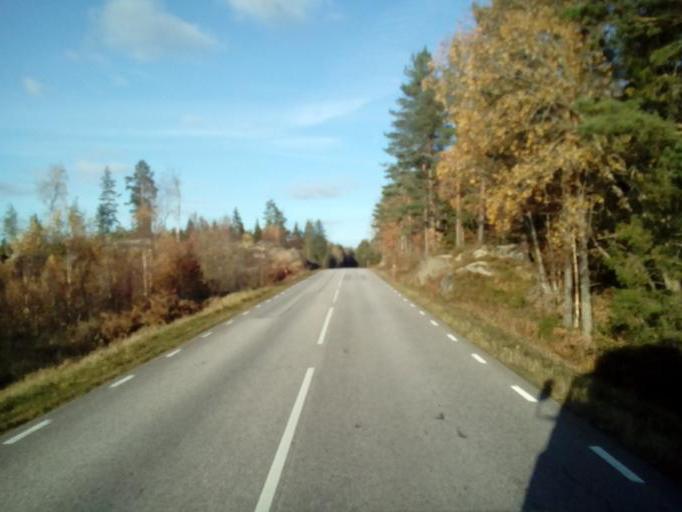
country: SE
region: Kalmar
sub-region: Vasterviks Kommun
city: Ankarsrum
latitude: 57.7433
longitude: 16.1100
